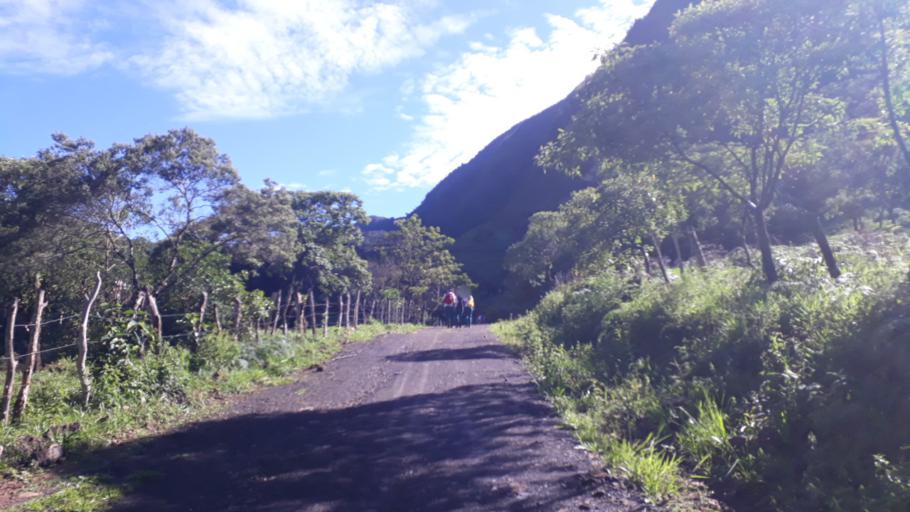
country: CO
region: Casanare
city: Nunchia
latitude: 5.6546
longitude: -72.4230
